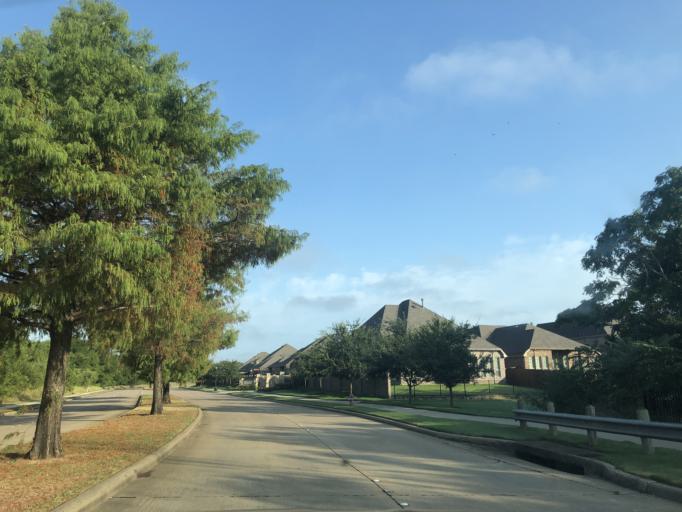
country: US
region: Texas
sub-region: Tarrant County
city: Euless
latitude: 32.8472
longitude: -97.0674
